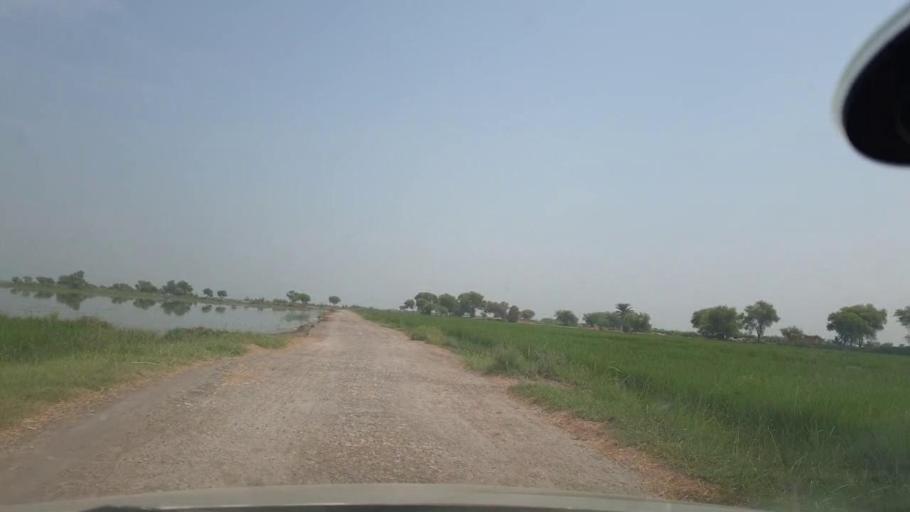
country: PK
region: Sindh
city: Jacobabad
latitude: 28.1381
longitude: 68.3712
